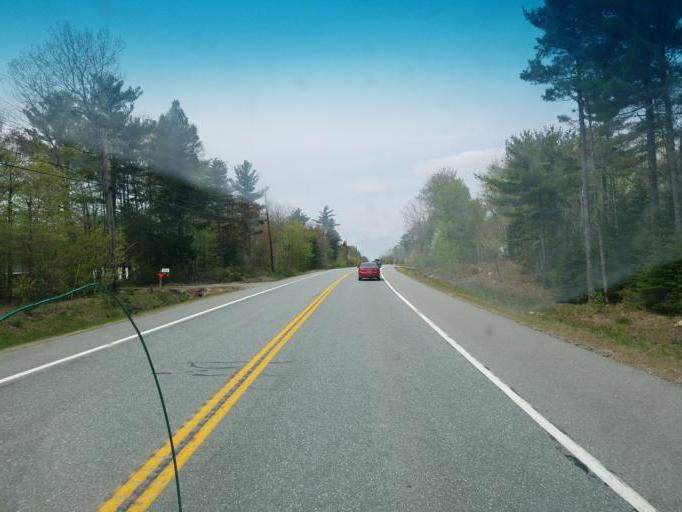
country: US
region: Maine
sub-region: Hancock County
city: Ellsworth
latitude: 44.5845
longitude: -68.4917
